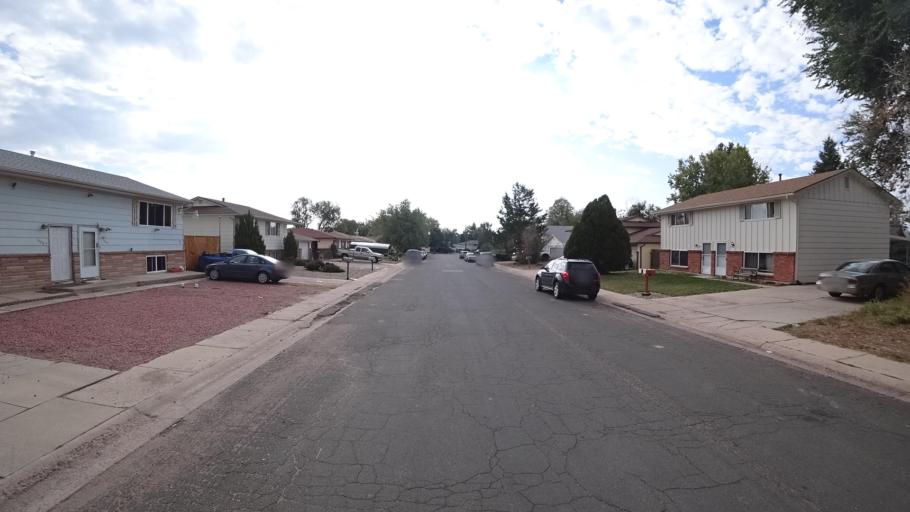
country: US
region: Colorado
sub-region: El Paso County
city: Cimarron Hills
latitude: 38.8524
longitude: -104.7511
